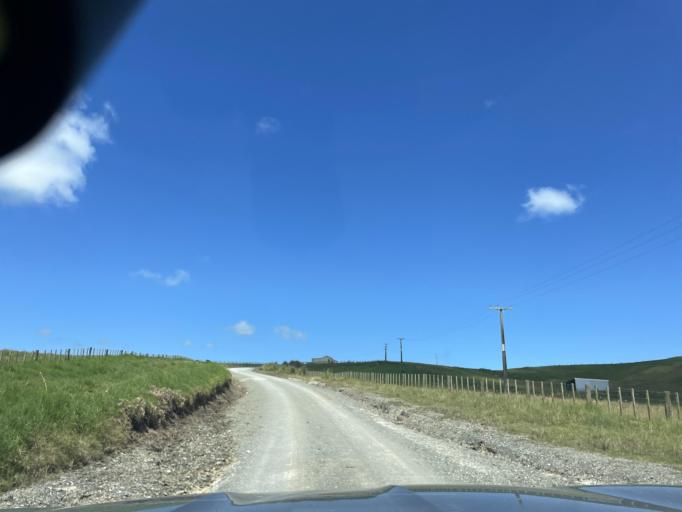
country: NZ
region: Auckland
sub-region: Auckland
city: Wellsford
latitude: -36.2858
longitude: 174.3538
